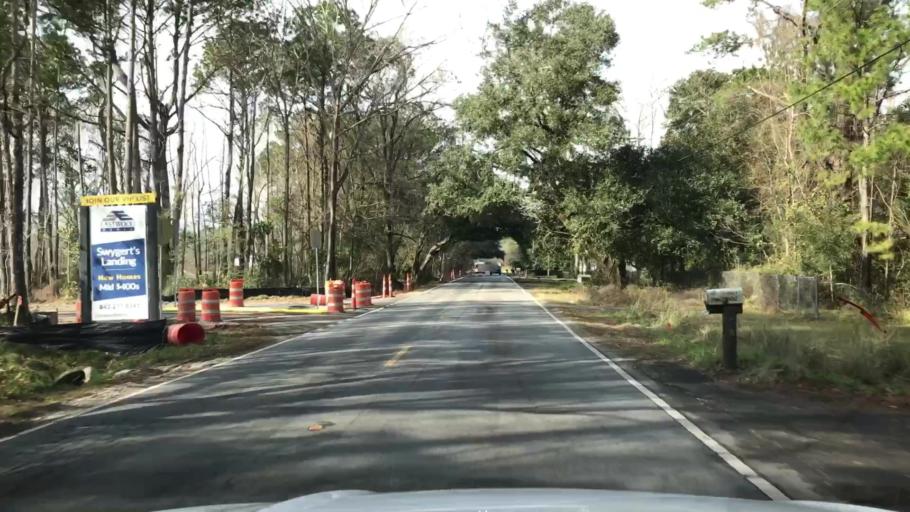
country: US
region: South Carolina
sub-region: Charleston County
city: Shell Point
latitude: 32.7660
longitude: -80.0667
